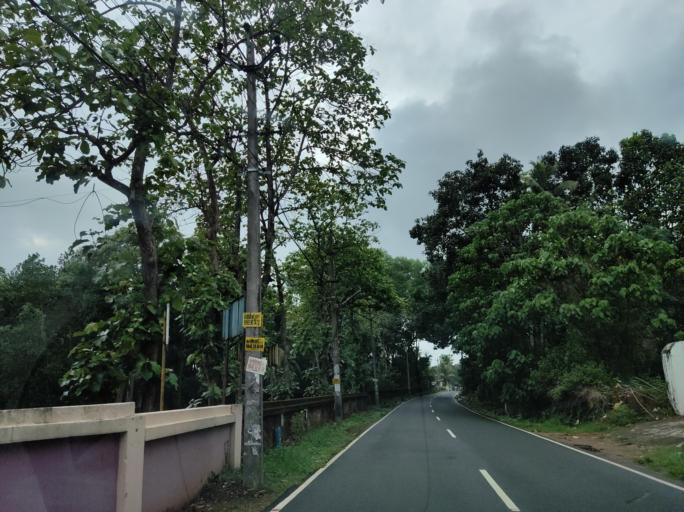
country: IN
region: Kerala
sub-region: Alappuzha
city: Mavelikara
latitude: 9.2348
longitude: 76.5612
